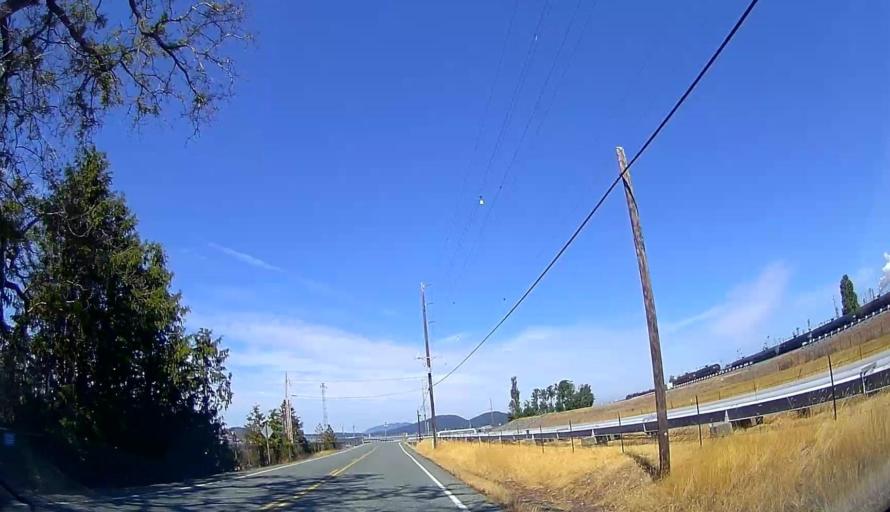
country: US
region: Washington
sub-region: Skagit County
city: Anacortes
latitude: 48.4866
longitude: -122.5753
